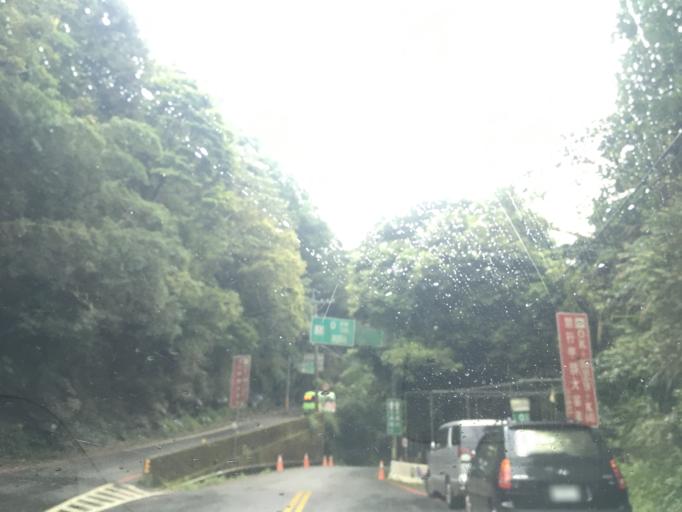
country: TW
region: Taiwan
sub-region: Yunlin
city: Douliu
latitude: 23.5601
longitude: 120.6083
